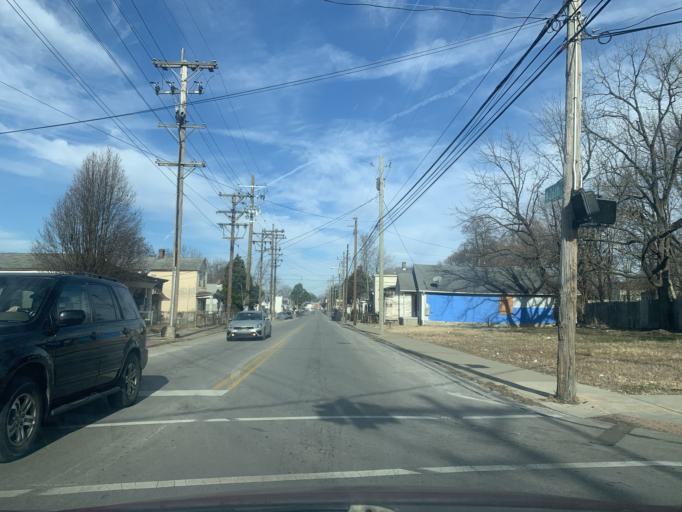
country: US
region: Kentucky
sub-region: Jefferson County
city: Louisville
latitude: 38.2608
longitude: -85.7935
